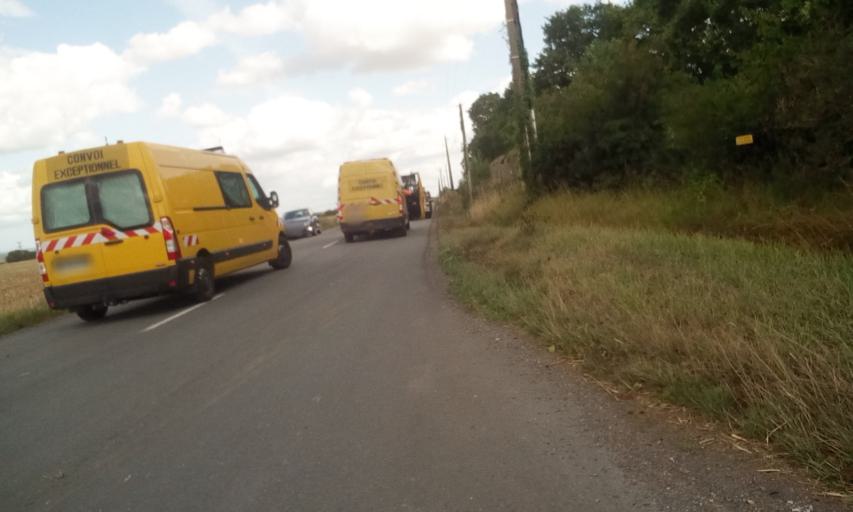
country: FR
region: Lower Normandy
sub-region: Departement du Calvados
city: Cagny
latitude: 49.1157
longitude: -0.2596
